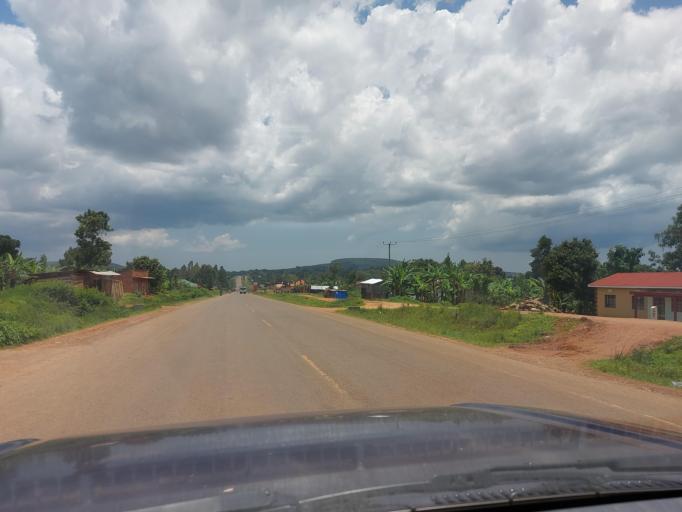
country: UG
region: Central Region
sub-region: Mukono District
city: Mukono
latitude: 0.2964
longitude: 32.7833
